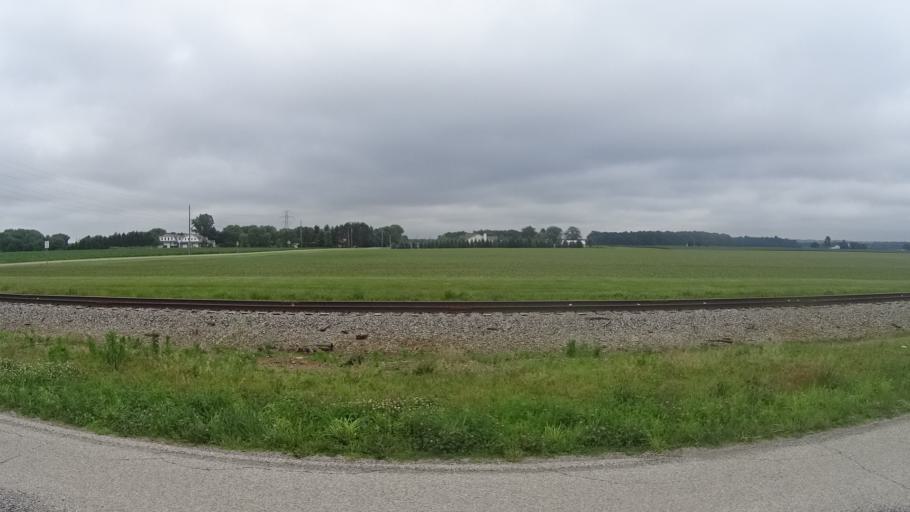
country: US
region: Ohio
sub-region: Erie County
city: Huron
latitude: 41.3574
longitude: -82.5444
